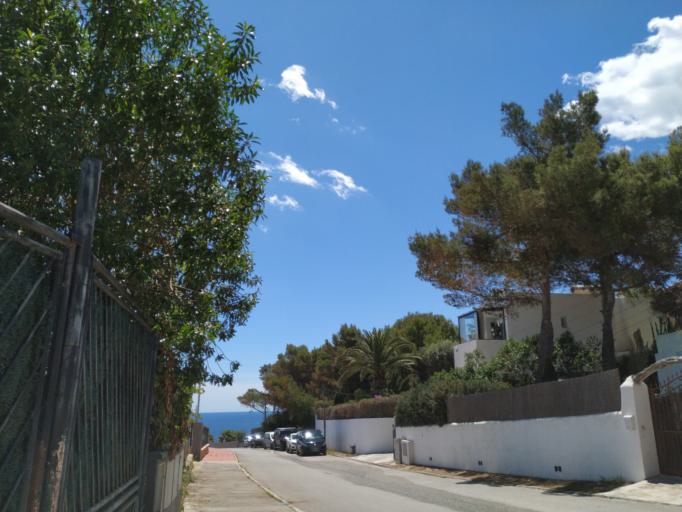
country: ES
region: Balearic Islands
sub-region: Illes Balears
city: Ibiza
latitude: 38.9179
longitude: 1.4738
